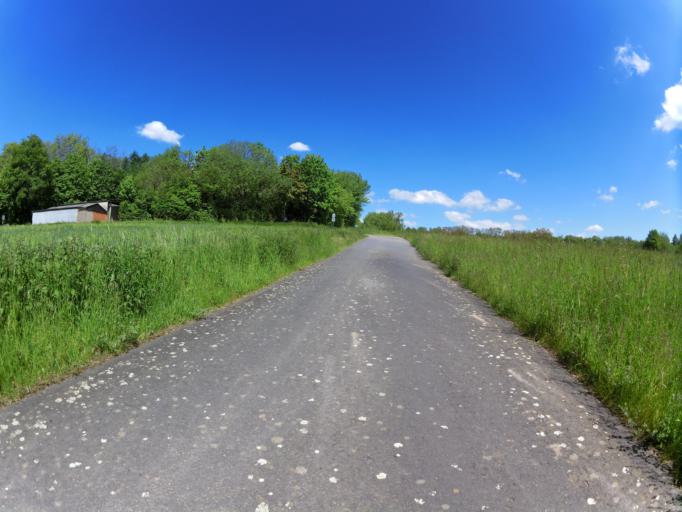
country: DE
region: Thuringia
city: Dankmarshausen
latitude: 50.9533
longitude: 10.0390
